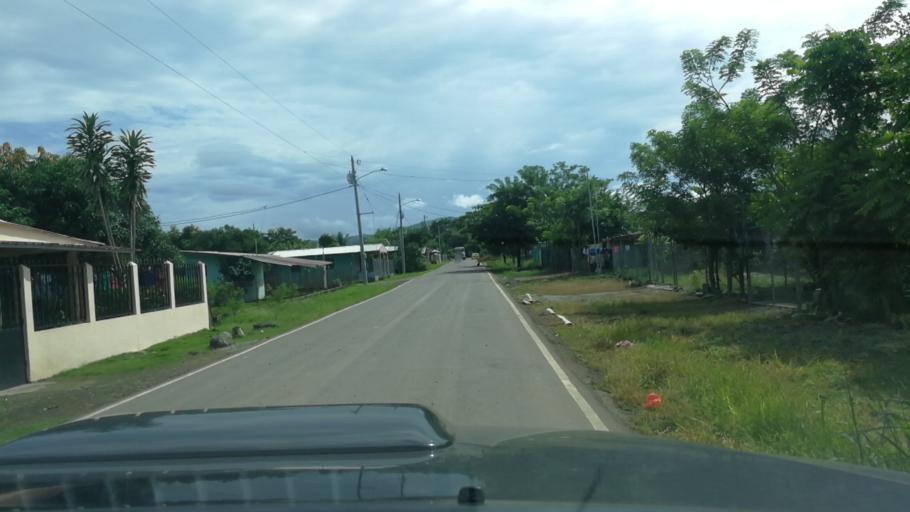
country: PA
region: Panama
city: Paso Blanco
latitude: 9.1351
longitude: -79.2533
